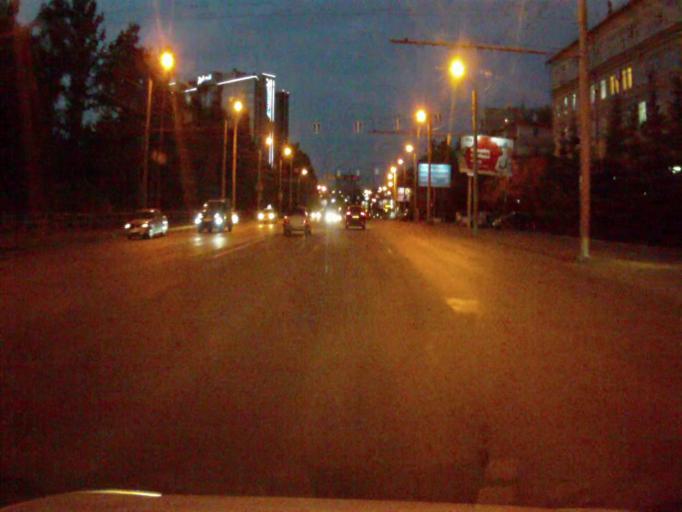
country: RU
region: Chelyabinsk
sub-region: Gorod Chelyabinsk
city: Chelyabinsk
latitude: 55.1648
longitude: 61.3809
